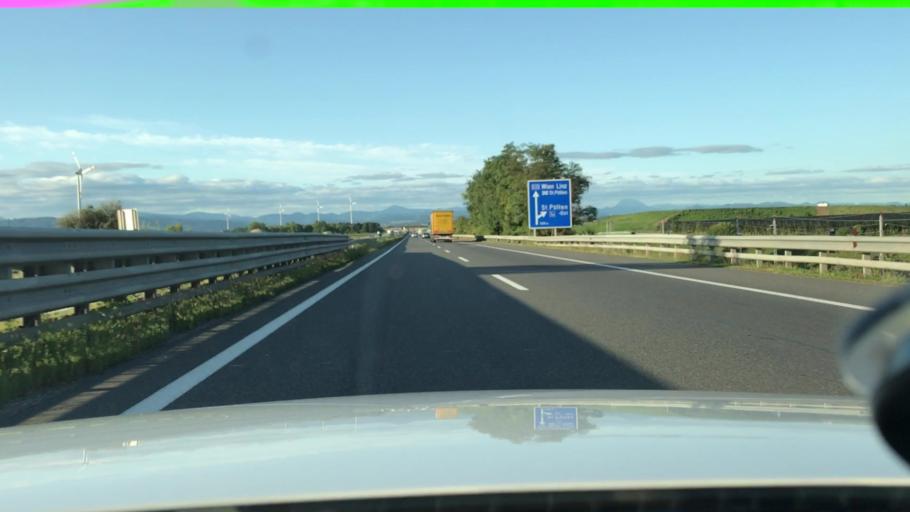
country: AT
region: Lower Austria
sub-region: Sankt Polten Stadt
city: Sankt Poelten
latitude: 48.2128
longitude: 15.6710
